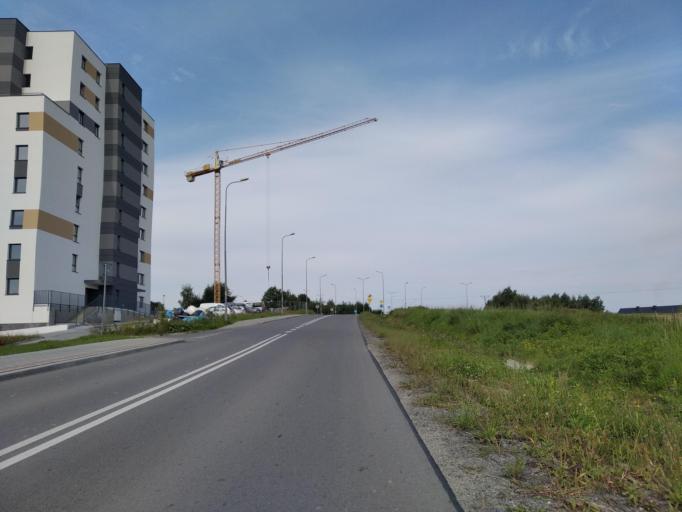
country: PL
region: Subcarpathian Voivodeship
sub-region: Powiat ropczycko-sedziszowski
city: Ropczyce
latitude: 50.0620
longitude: 21.6109
